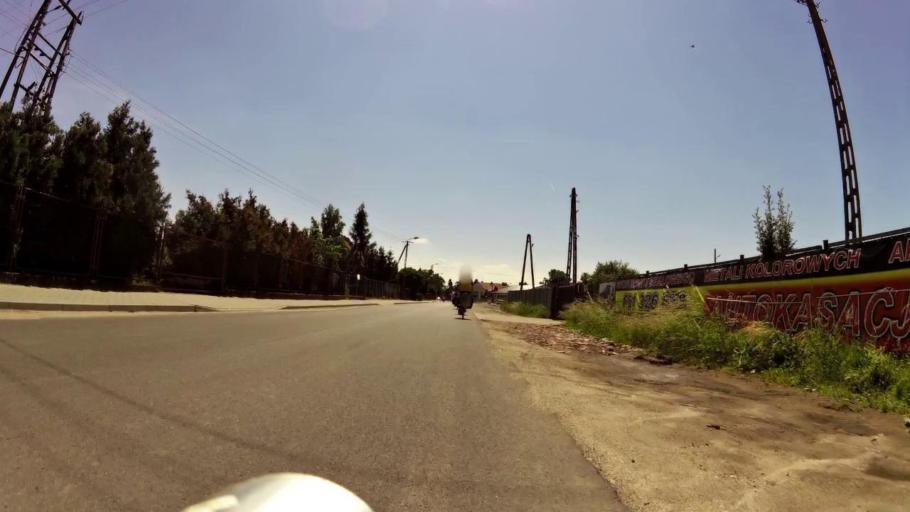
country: PL
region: Kujawsko-Pomorskie
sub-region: Powiat nakielski
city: Slesin
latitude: 53.1667
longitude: 17.7040
